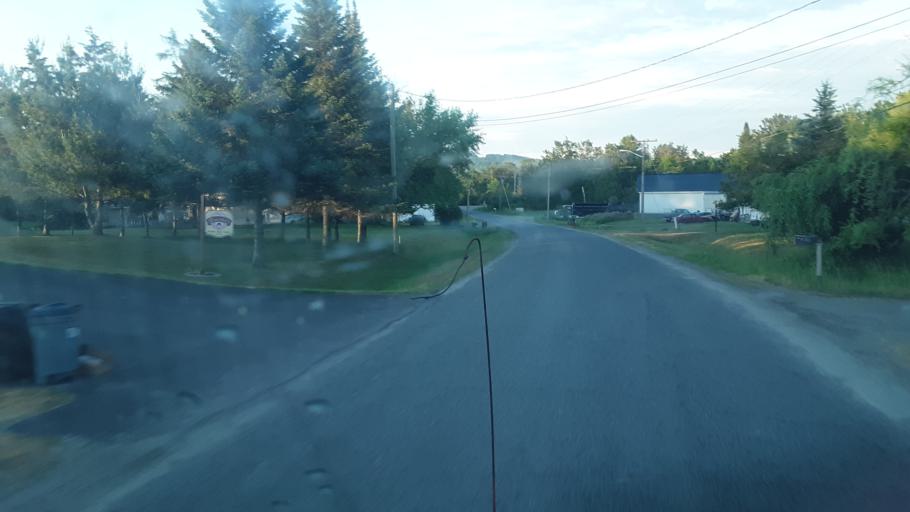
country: US
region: Maine
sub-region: Aroostook County
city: Presque Isle
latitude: 46.7569
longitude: -68.1022
